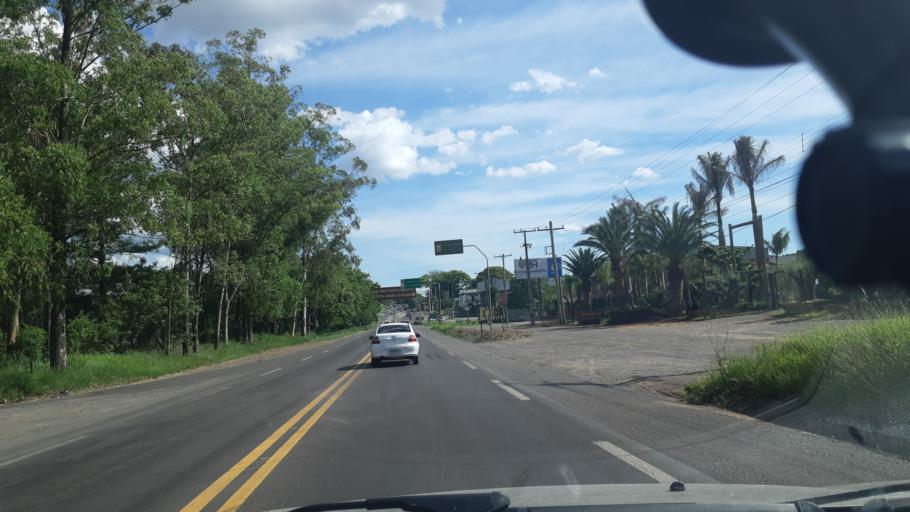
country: BR
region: Rio Grande do Sul
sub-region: Estancia Velha
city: Estancia Velha
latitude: -29.6458
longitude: -51.1434
